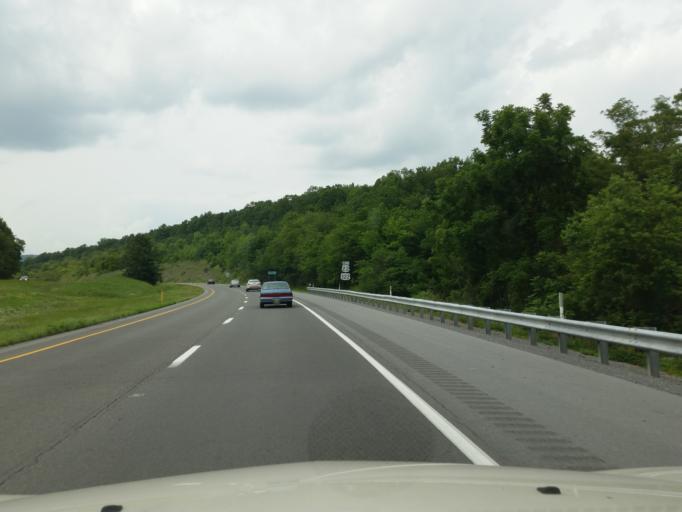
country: US
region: Pennsylvania
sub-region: Juniata County
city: Mifflintown
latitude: 40.5898
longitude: -77.3743
